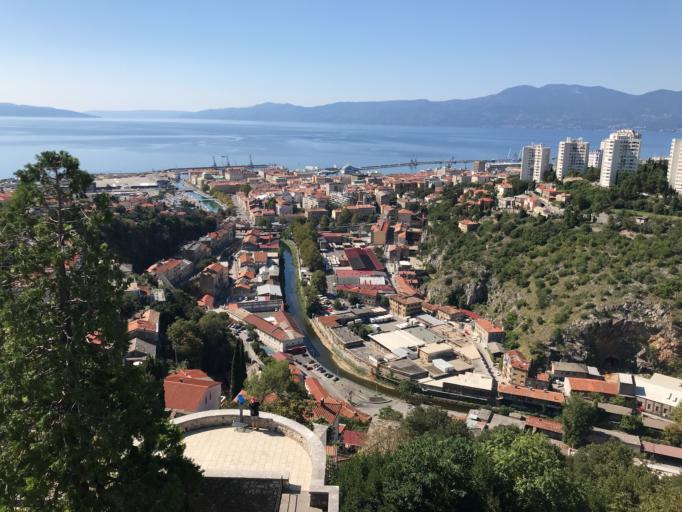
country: HR
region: Primorsko-Goranska
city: Drenova
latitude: 45.3325
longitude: 14.4554
